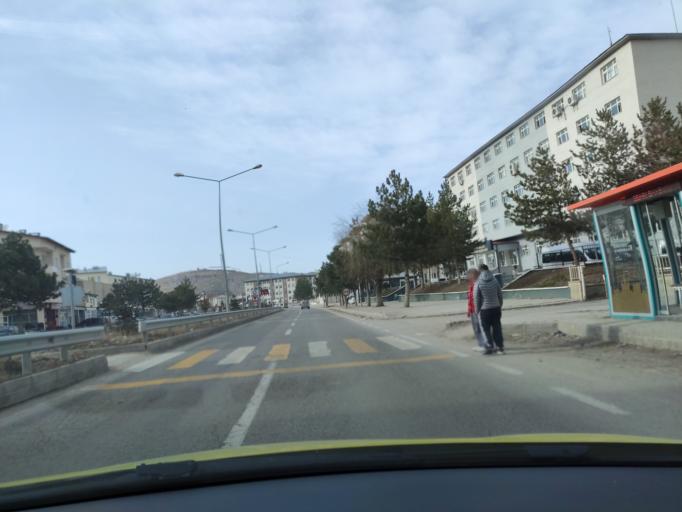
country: TR
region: Bayburt
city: Bayburt
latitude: 40.2473
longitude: 40.2333
